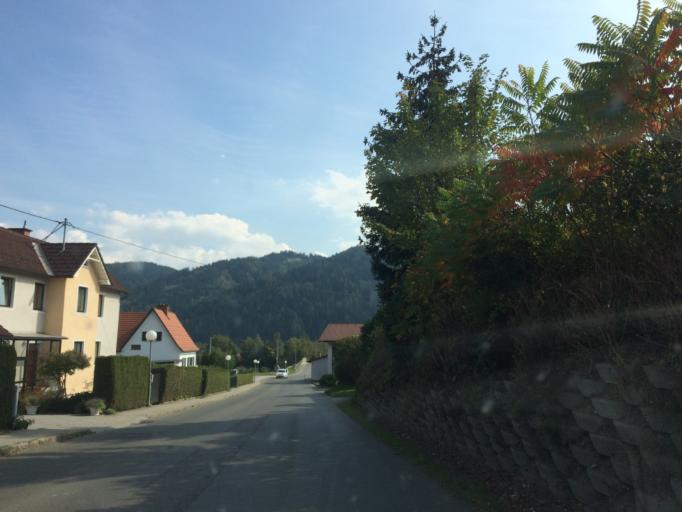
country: AT
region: Styria
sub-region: Politischer Bezirk Leoben
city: Kraubath an der Mur
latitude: 47.3046
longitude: 14.9411
